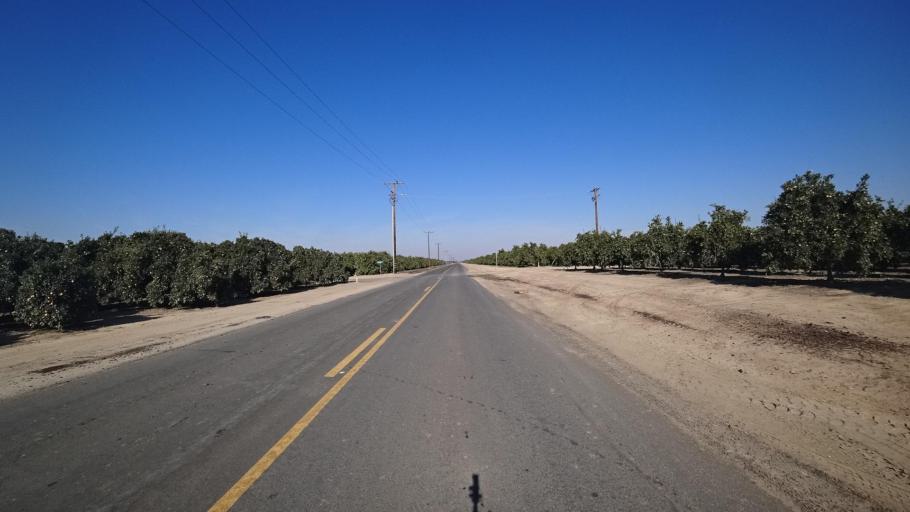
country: US
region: California
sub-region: Tulare County
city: Richgrove
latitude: 35.7249
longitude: -119.1340
